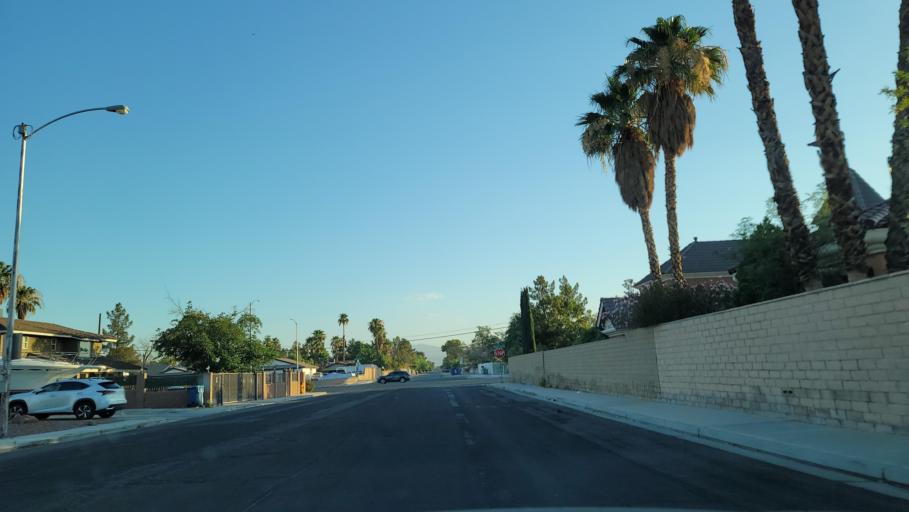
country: US
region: Nevada
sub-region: Clark County
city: Spring Valley
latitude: 36.1284
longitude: -115.2294
